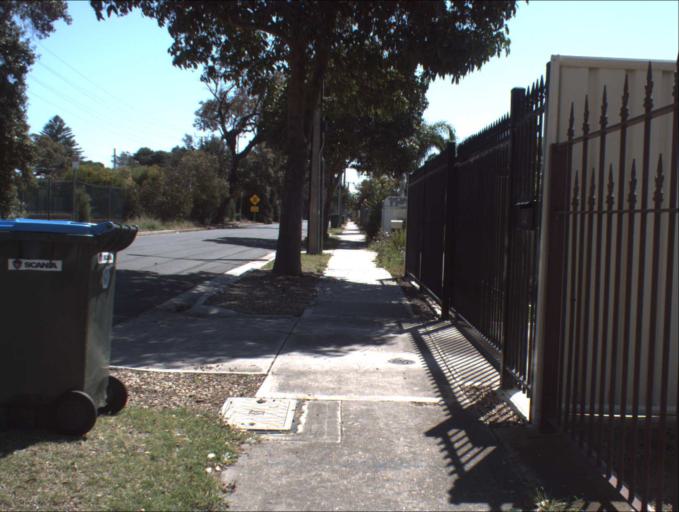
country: AU
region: South Australia
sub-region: Port Adelaide Enfield
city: Birkenhead
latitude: -34.8137
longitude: 138.4992
